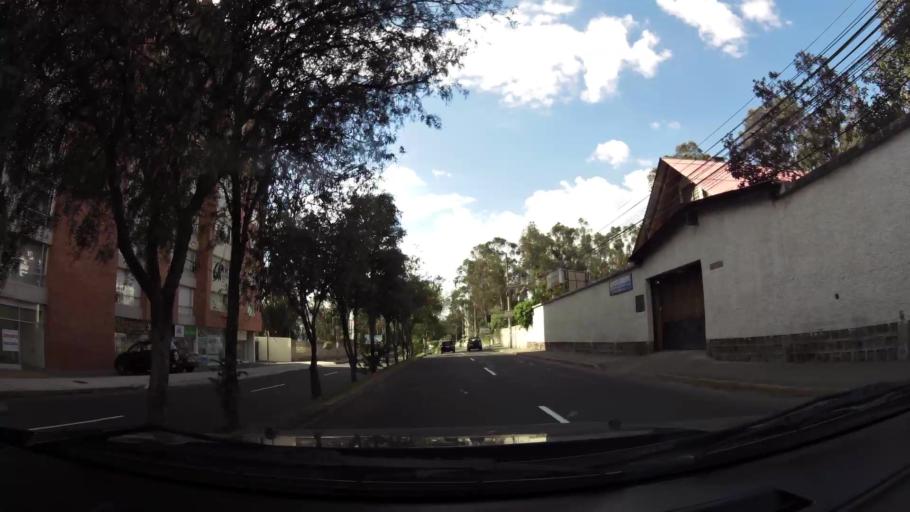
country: EC
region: Pichincha
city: Quito
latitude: -0.1114
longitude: -78.4825
